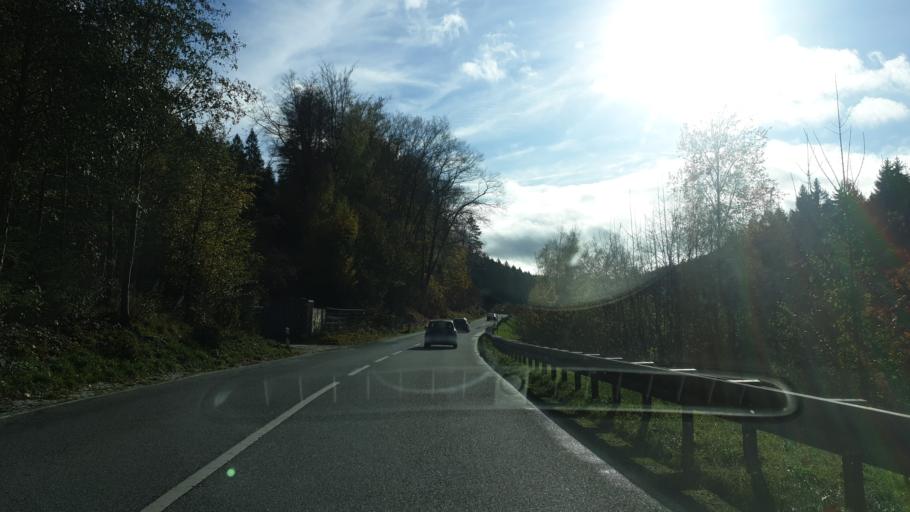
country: DE
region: Saxony
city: Bockau
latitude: 50.5692
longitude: 12.6932
